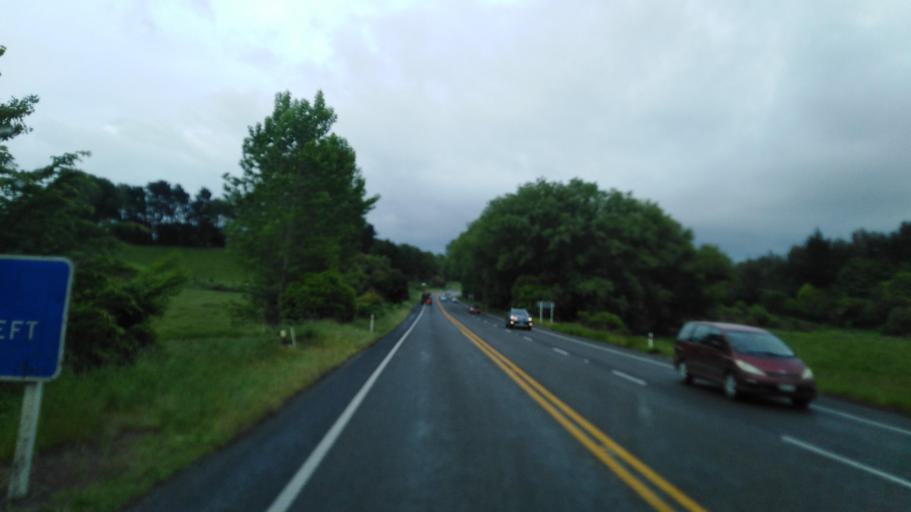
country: NZ
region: Wellington
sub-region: Kapiti Coast District
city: Otaki
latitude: -40.7383
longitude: 175.1839
